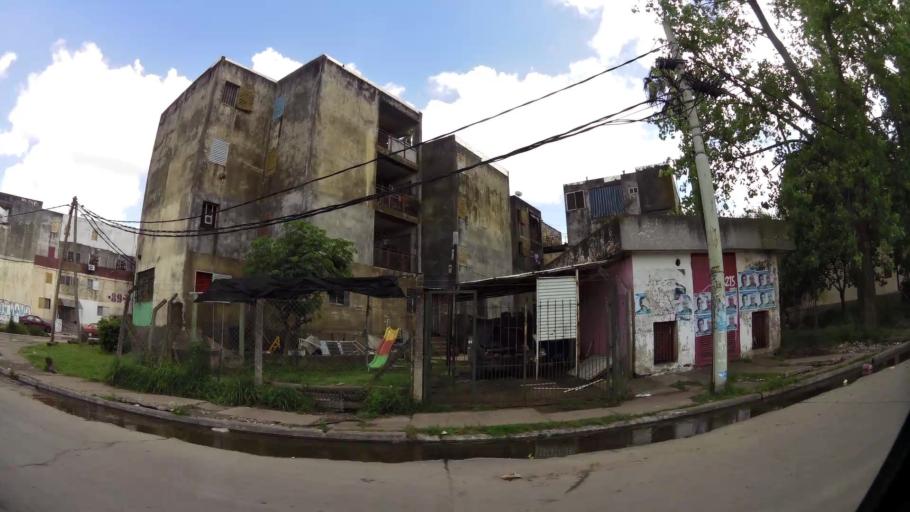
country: AR
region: Buenos Aires
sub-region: Partido de Quilmes
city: Quilmes
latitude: -34.8341
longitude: -58.2210
